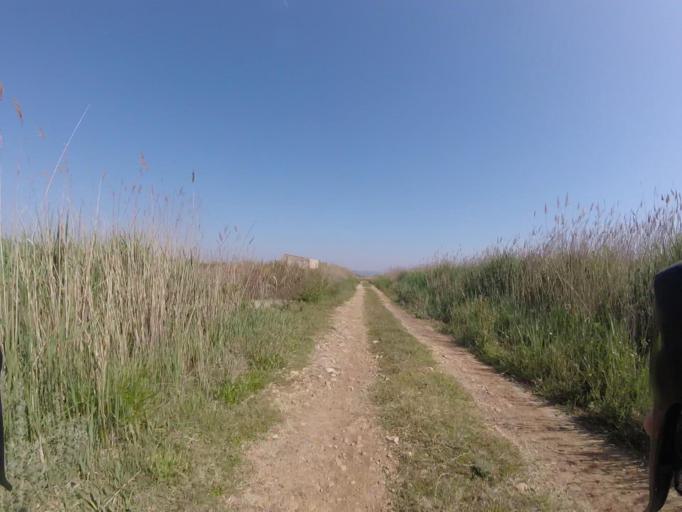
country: ES
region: Valencia
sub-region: Provincia de Castello
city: Torreblanca
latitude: 40.1639
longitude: 0.1724
